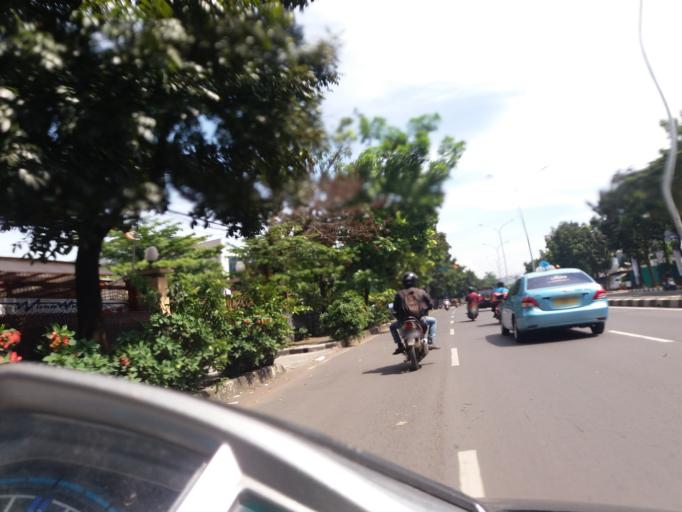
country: ID
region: West Java
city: Bandung
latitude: -6.9490
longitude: 107.6304
